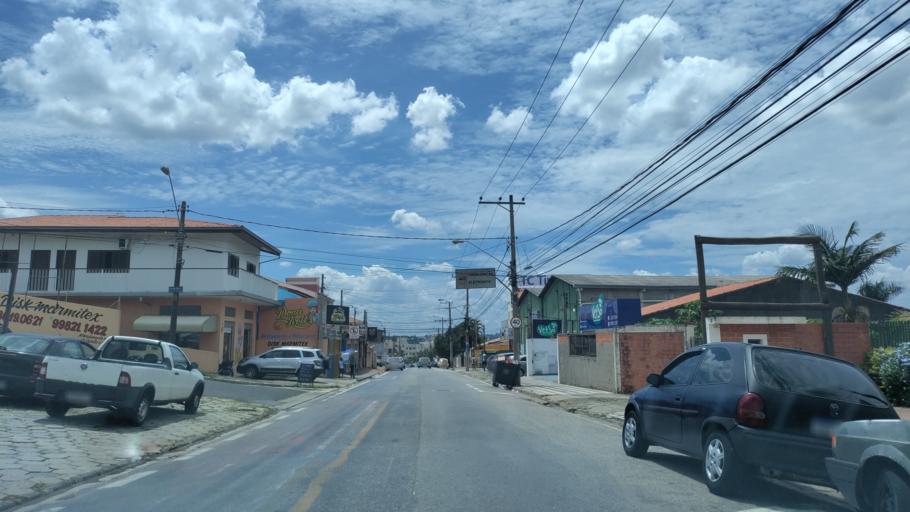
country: BR
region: Sao Paulo
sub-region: Sorocaba
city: Sorocaba
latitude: -23.4774
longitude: -47.4615
